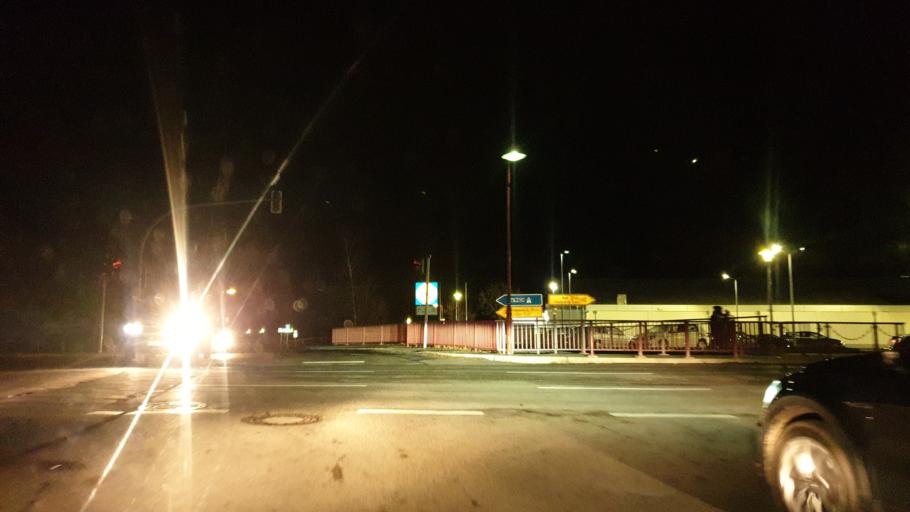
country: DE
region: Saxony
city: Lugau
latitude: 50.7213
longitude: 12.7549
